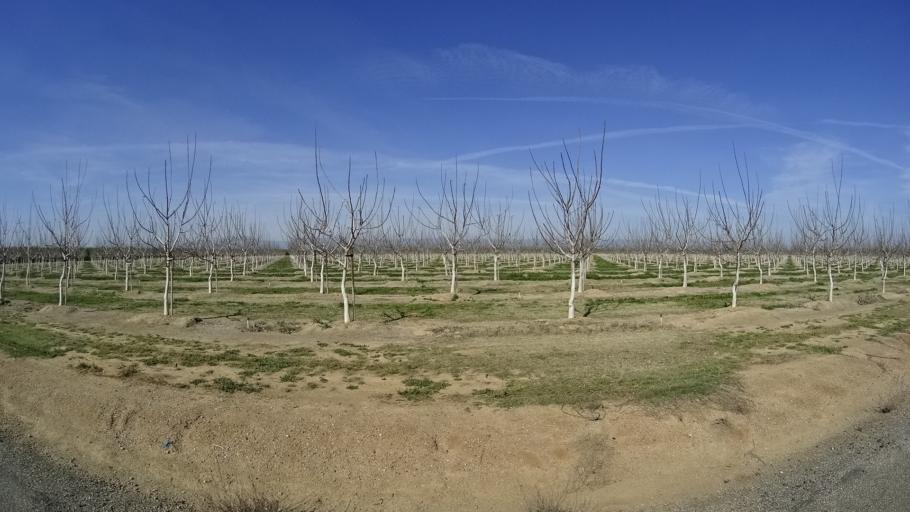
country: US
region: California
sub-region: Glenn County
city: Willows
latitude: 39.6129
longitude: -122.2128
